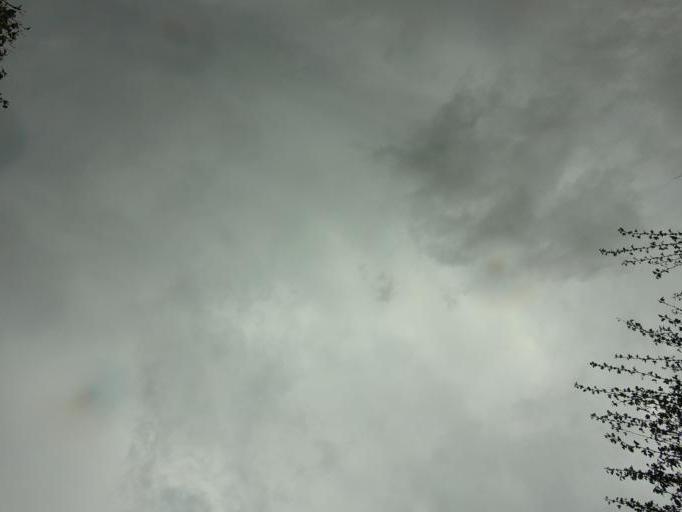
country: GB
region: England
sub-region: Cambridgeshire
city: Duxford
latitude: 52.0564
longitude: 0.1251
